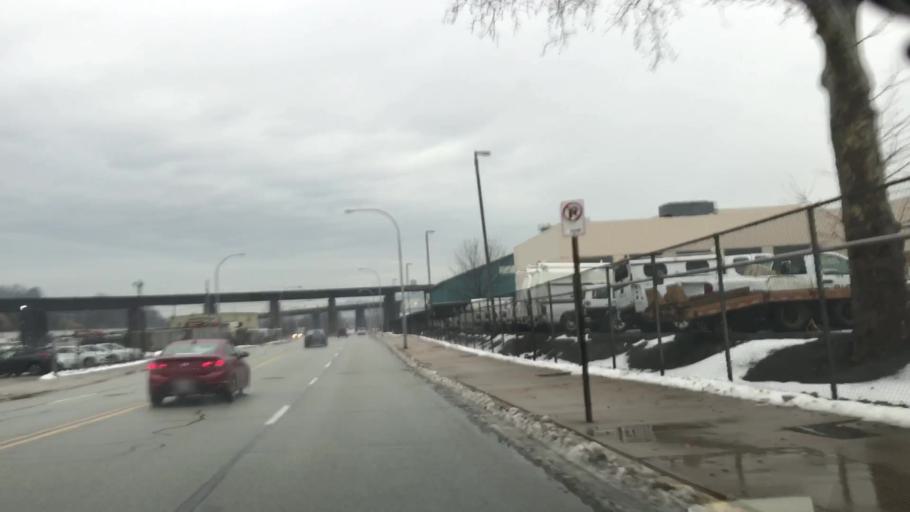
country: US
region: Pennsylvania
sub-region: Allegheny County
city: McKees Rocks
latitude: 40.4693
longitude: -80.0387
